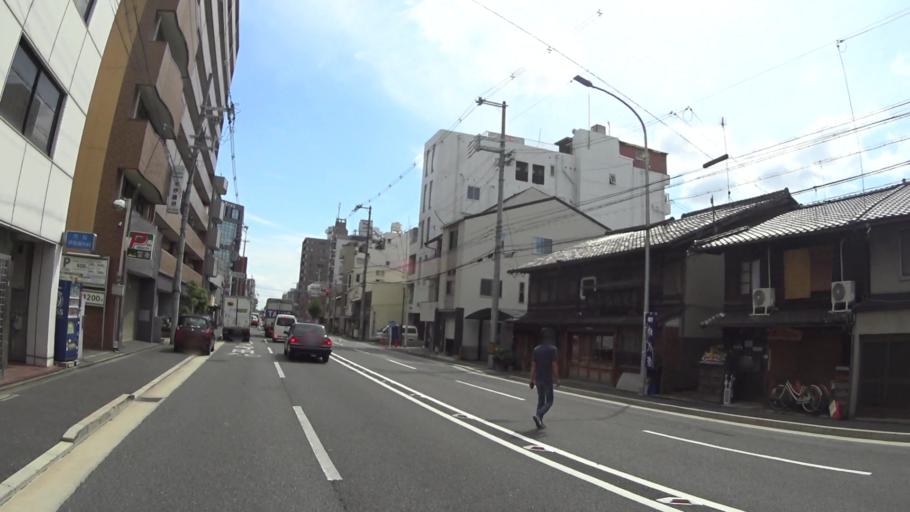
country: JP
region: Kyoto
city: Kyoto
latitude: 34.9975
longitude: 135.7492
